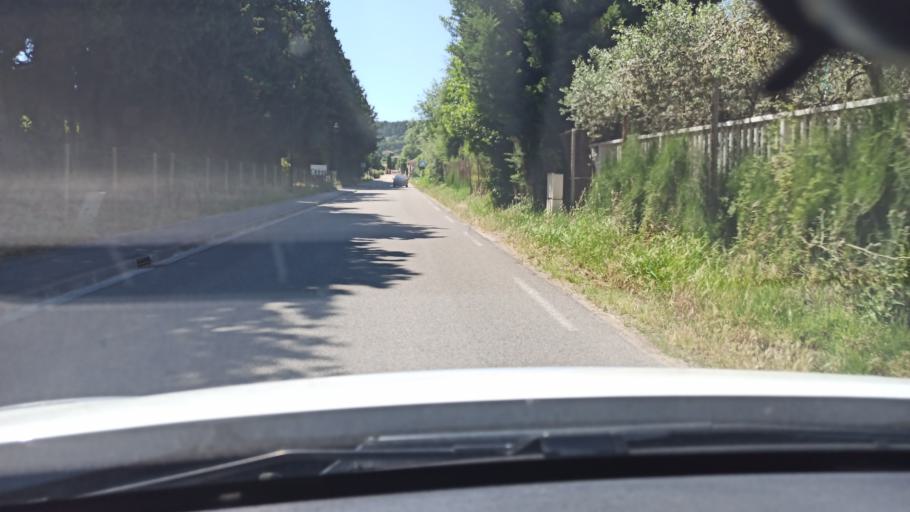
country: FR
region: Provence-Alpes-Cote d'Azur
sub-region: Departement des Bouches-du-Rhone
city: Noves
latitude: 43.8761
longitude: 4.8975
